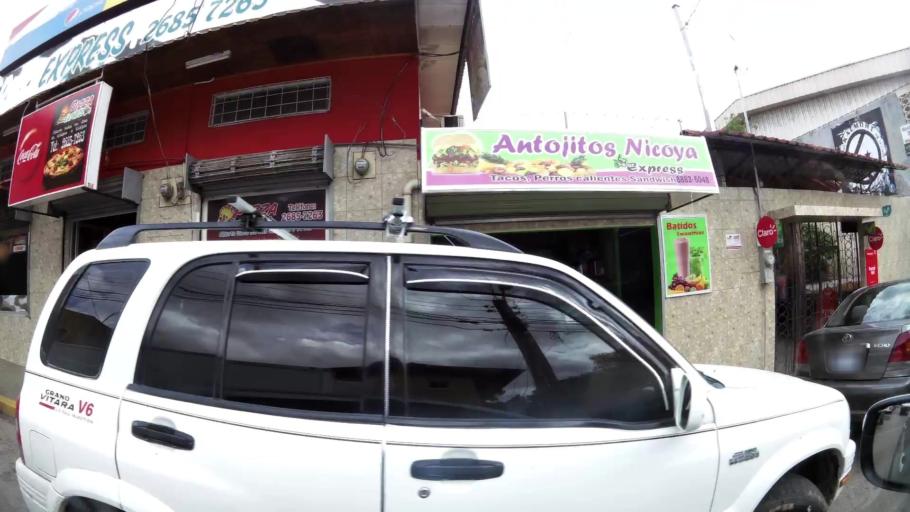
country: CR
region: Guanacaste
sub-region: Canton de Nicoya
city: Nicoya
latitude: 10.1421
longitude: -85.4528
